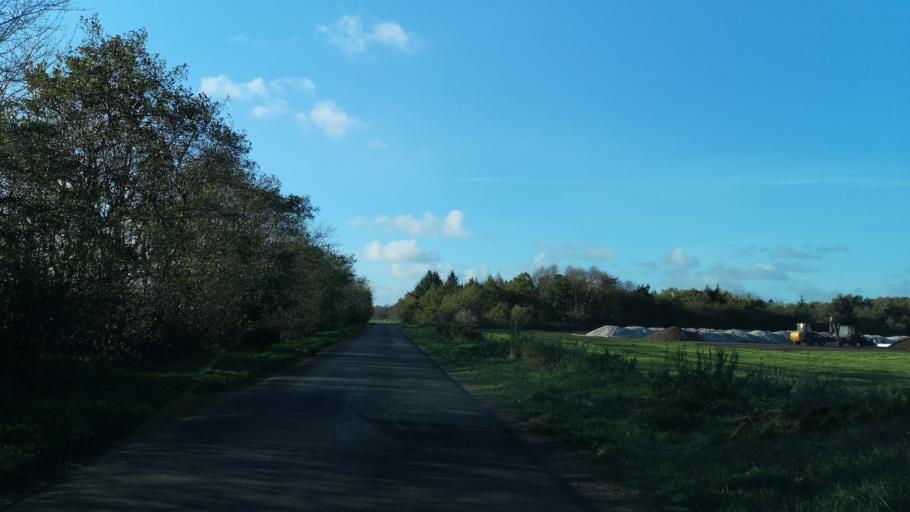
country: DK
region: Central Jutland
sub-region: Ringkobing-Skjern Kommune
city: Tarm
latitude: 55.8266
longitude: 8.3958
